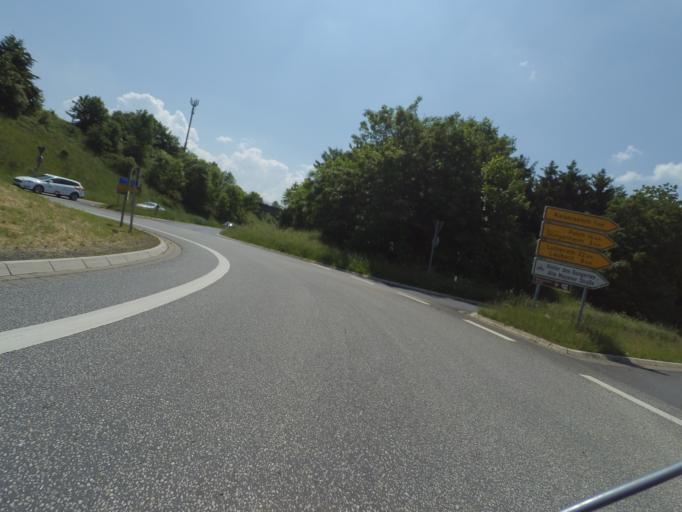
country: DE
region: Rheinland-Pfalz
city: Kaisersesch
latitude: 50.2340
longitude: 7.1473
